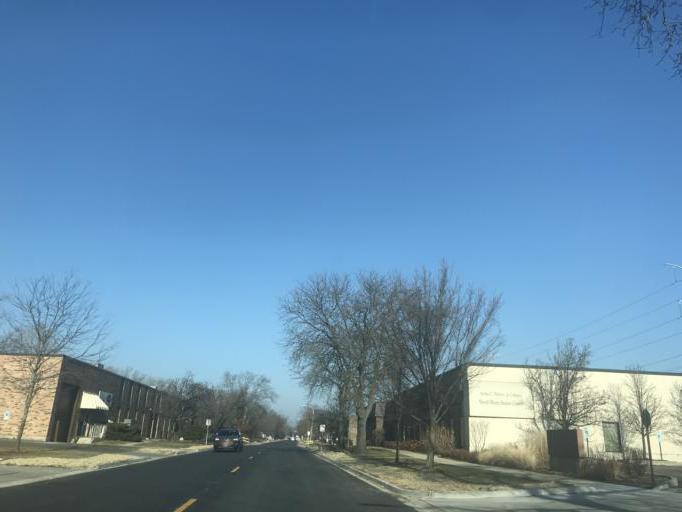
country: US
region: Illinois
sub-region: Cook County
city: Northfield
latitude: 42.0953
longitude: -87.7705
